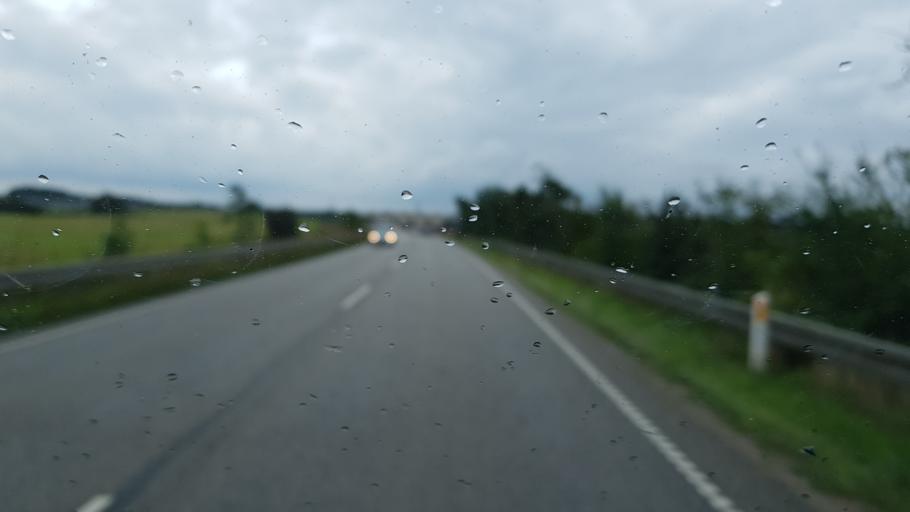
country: DK
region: Central Jutland
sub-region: Horsens Kommune
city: Horsens
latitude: 55.8902
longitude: 9.7660
